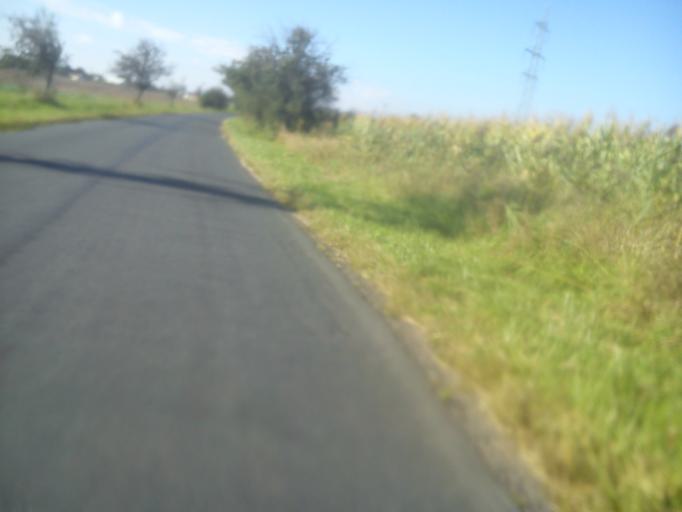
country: CZ
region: South Moravian
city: Telnice
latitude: 49.1008
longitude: 16.7397
